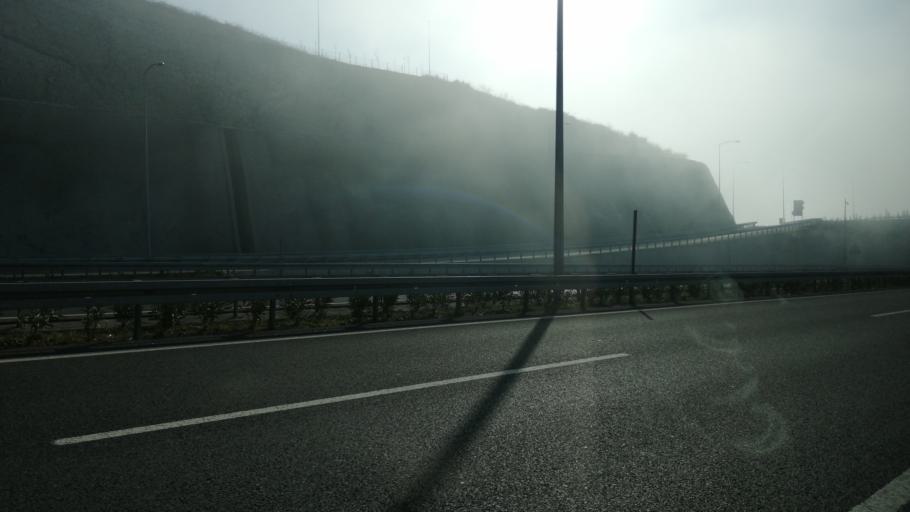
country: TR
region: Kocaeli
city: Tavsanli
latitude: 40.7778
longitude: 29.5180
